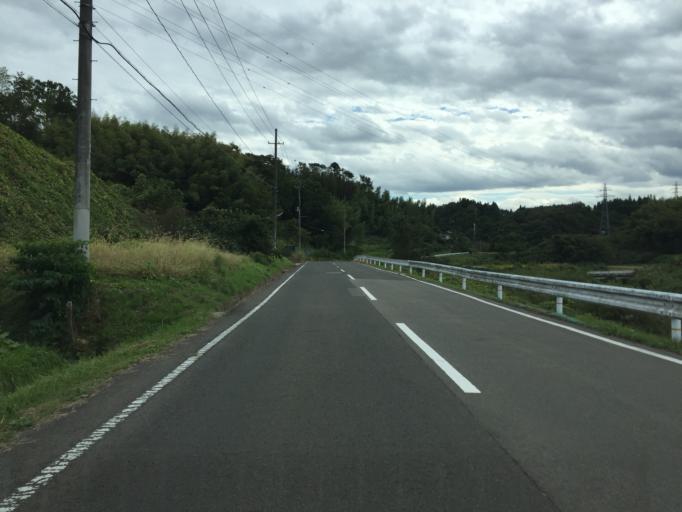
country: JP
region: Fukushima
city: Fukushima-shi
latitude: 37.6944
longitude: 140.4907
